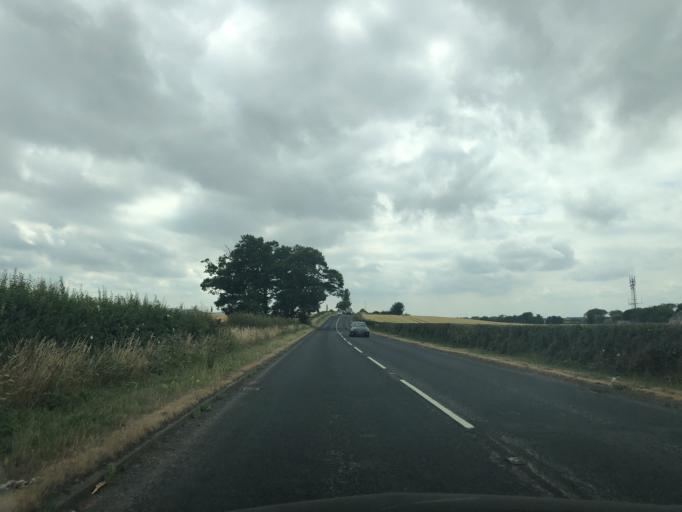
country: GB
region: England
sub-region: North Yorkshire
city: Great Ayton
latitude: 54.4789
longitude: -1.1539
